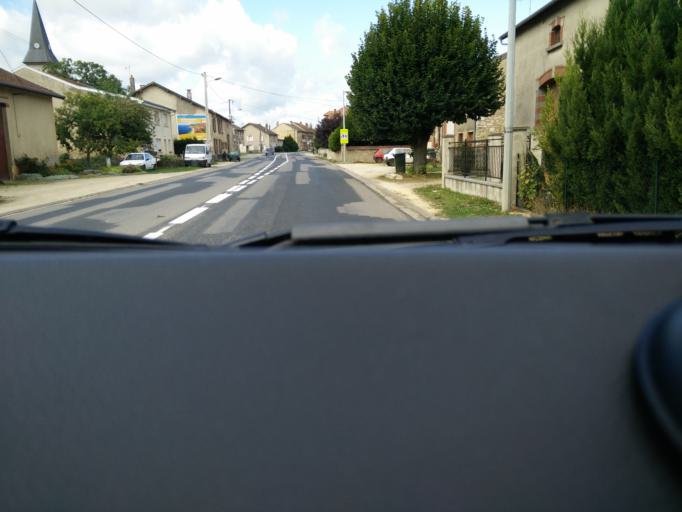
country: FR
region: Lorraine
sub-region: Departement de la Meuse
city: Etain
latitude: 49.1114
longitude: 5.6000
